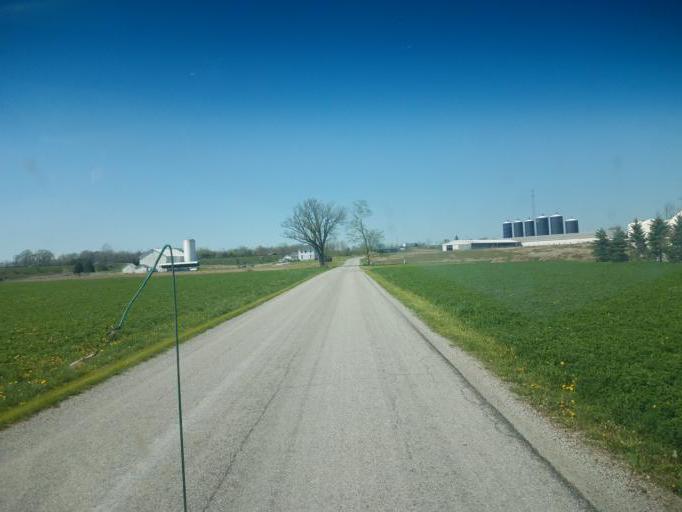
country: US
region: Ohio
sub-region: Medina County
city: Lodi
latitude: 40.9824
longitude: -82.0354
